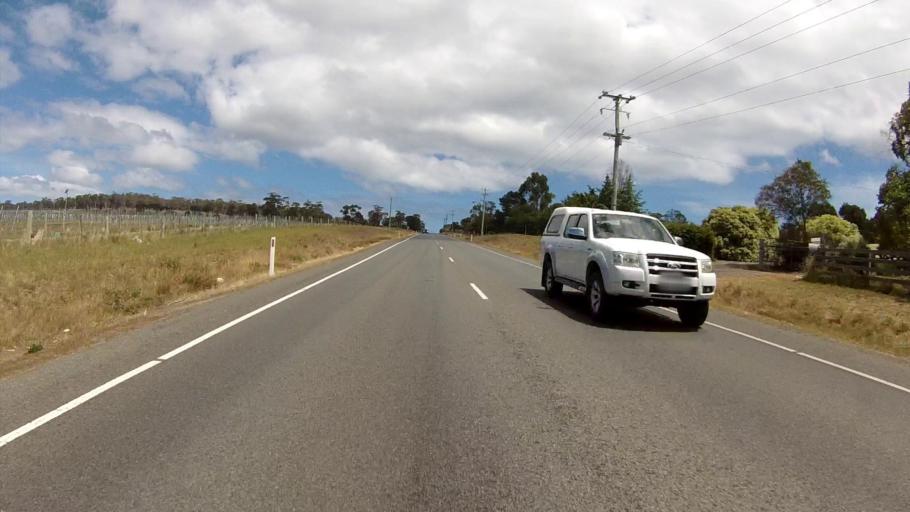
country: AU
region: Tasmania
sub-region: Sorell
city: Sorell
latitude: -42.8131
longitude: 147.6256
